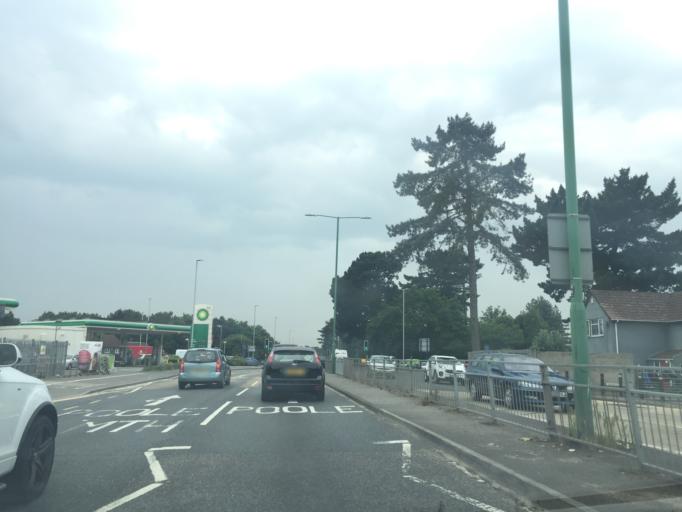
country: GB
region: England
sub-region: Dorset
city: Parkstone
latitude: 50.7546
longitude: -1.9312
